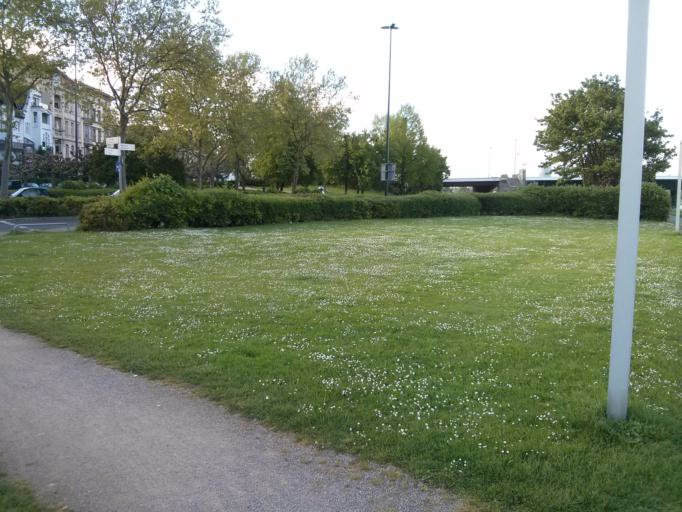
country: DE
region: North Rhine-Westphalia
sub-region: Regierungsbezirk Dusseldorf
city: Dusseldorf
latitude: 51.2300
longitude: 6.7628
